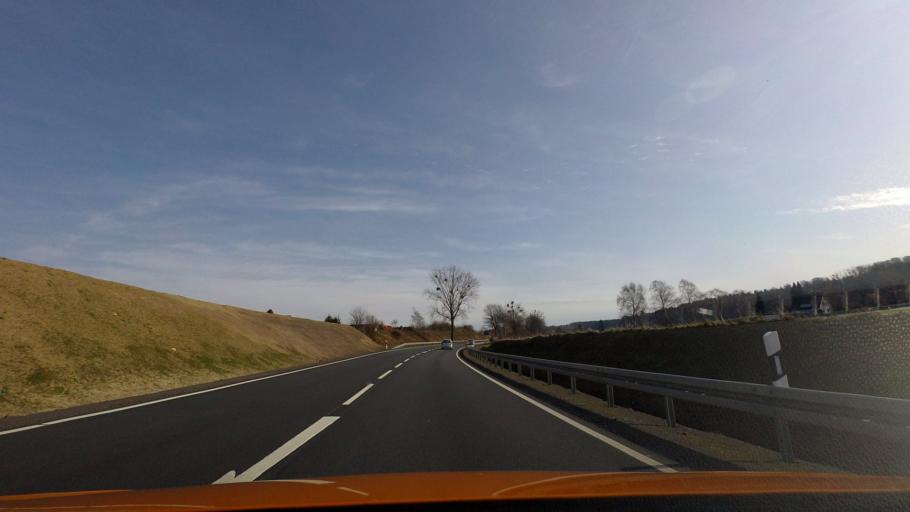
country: DE
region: Lower Saxony
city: Heuerssen
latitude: 52.3369
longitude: 9.2877
